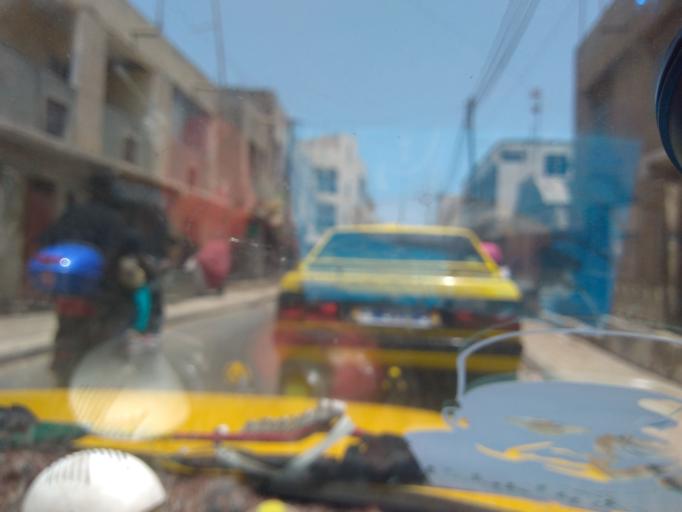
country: SN
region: Dakar
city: Grand Dakar
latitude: 14.7413
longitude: -17.4484
